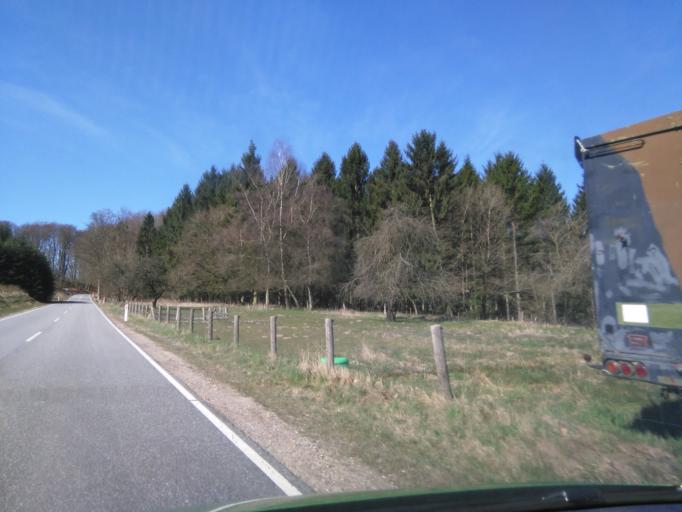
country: DK
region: Central Jutland
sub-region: Horsens Kommune
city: Braedstrup
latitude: 56.0158
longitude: 9.6650
